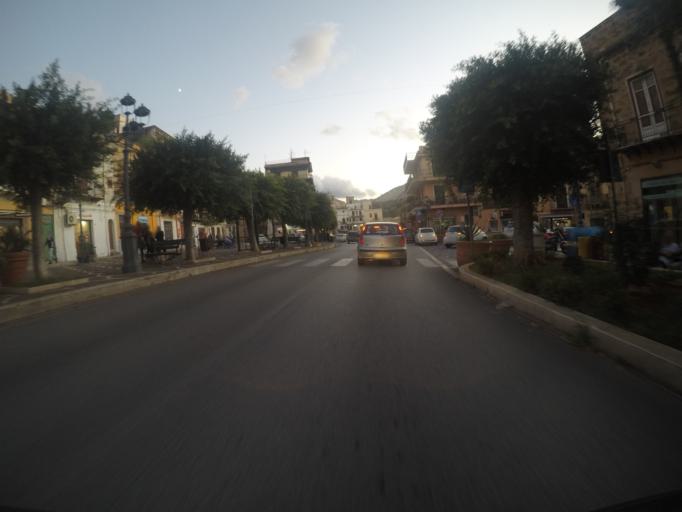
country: IT
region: Sicily
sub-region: Palermo
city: Capaci
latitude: 38.1715
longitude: 13.2397
